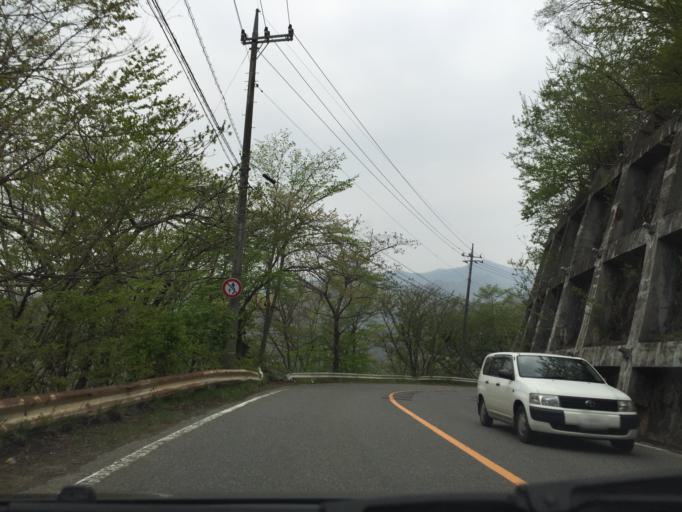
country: JP
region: Tochigi
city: Nikko
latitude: 36.9421
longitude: 139.6982
